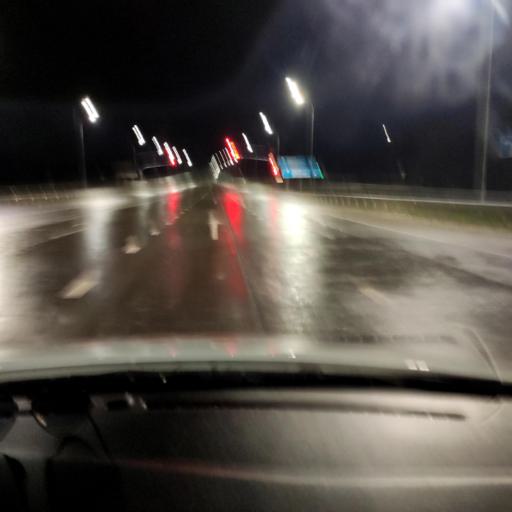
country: RU
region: Tatarstan
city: Stolbishchi
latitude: 55.6396
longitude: 49.1143
